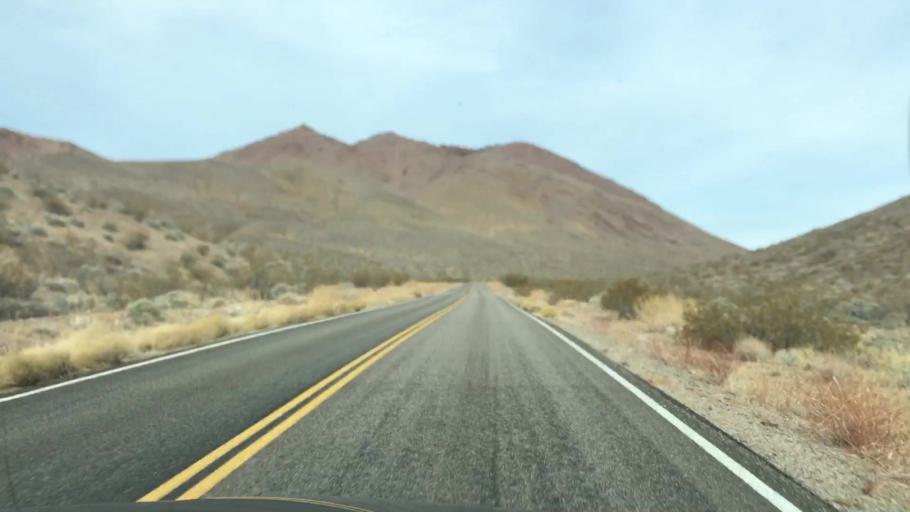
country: US
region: Nevada
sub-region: Nye County
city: Beatty
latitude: 36.7714
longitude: -116.9312
